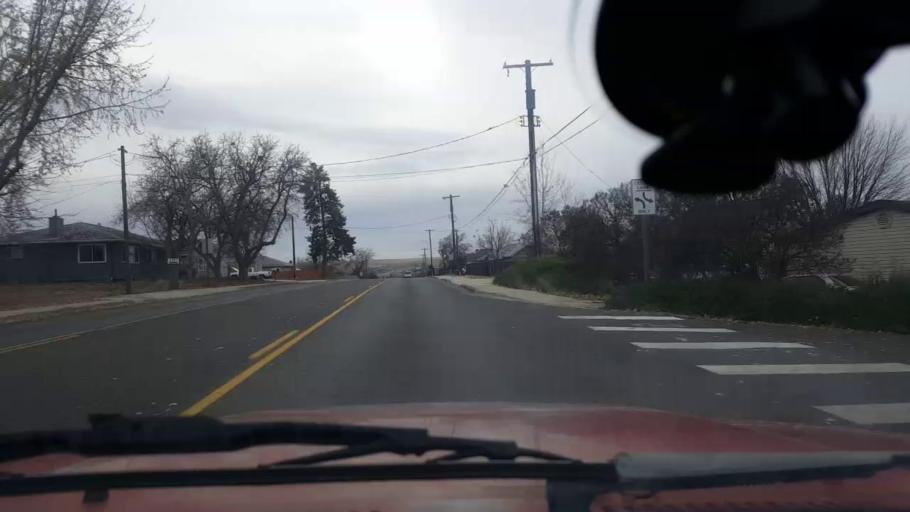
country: US
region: Washington
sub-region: Asotin County
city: Clarkston Heights-Vineland
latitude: 46.4003
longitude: -117.0807
